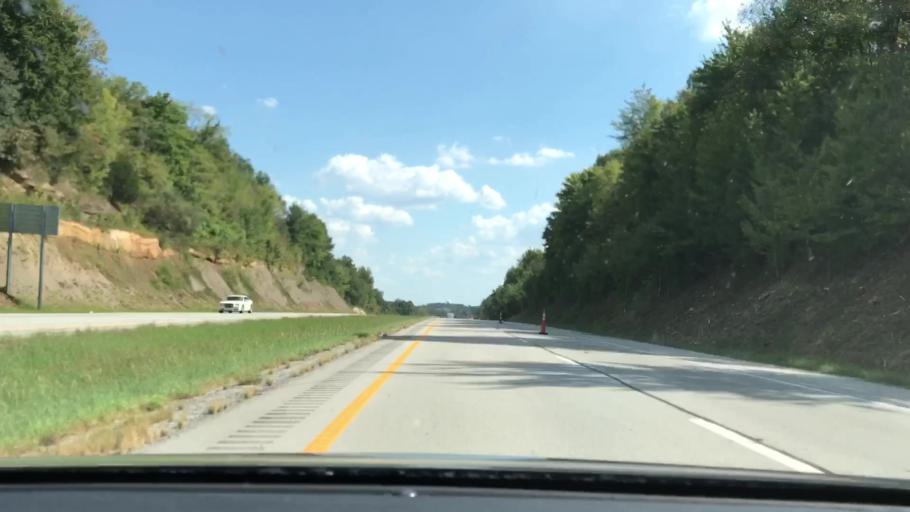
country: US
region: Kentucky
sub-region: Butler County
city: Morgantown
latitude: 37.2265
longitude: -86.7217
